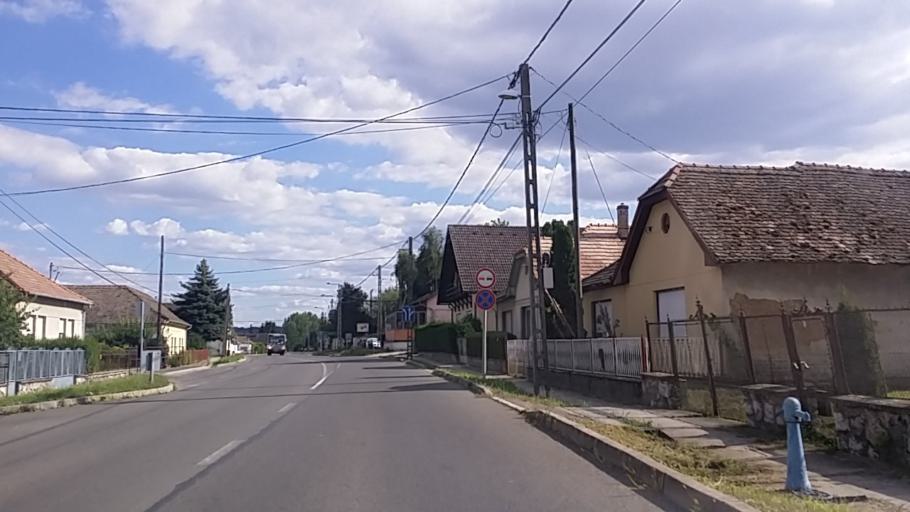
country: HU
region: Tolna
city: Dombovar
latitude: 46.3302
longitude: 18.1281
